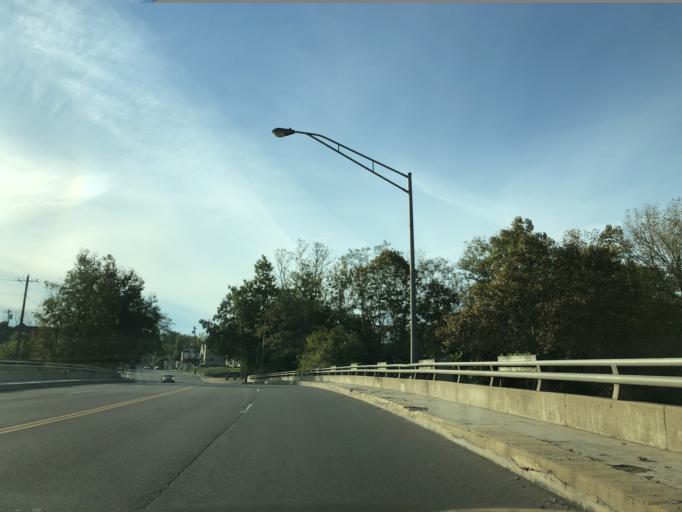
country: US
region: Ohio
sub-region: Hamilton County
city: Loveland
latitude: 39.2686
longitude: -84.2600
